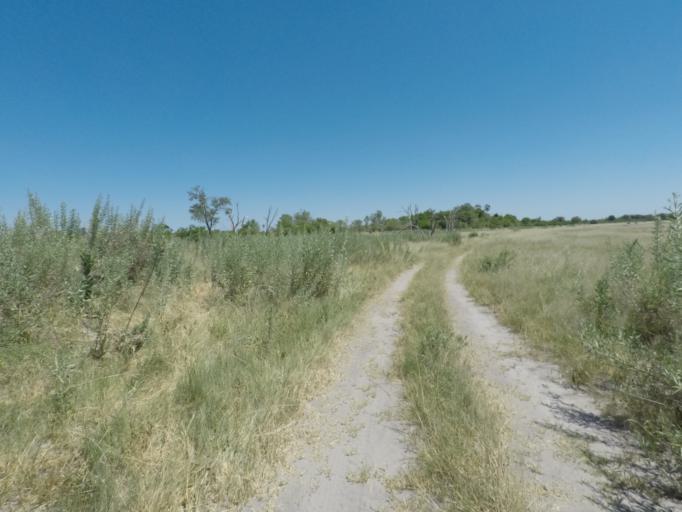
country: BW
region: North West
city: Maun
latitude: -19.4756
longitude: 23.5529
